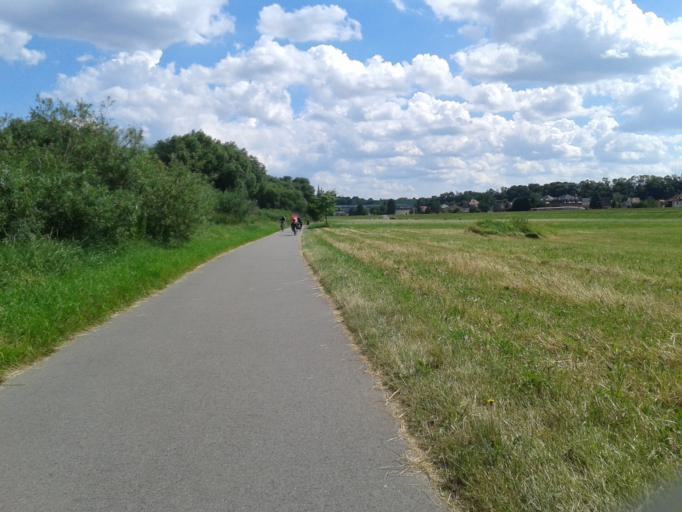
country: DE
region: Saxony
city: Radebeul
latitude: 51.0814
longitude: 13.6662
